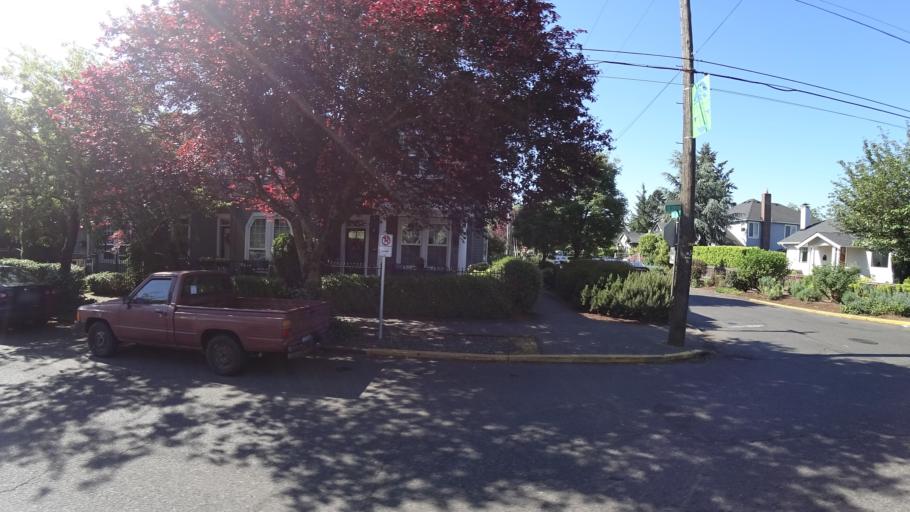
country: US
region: Oregon
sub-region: Multnomah County
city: Portland
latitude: 45.5483
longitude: -122.6155
